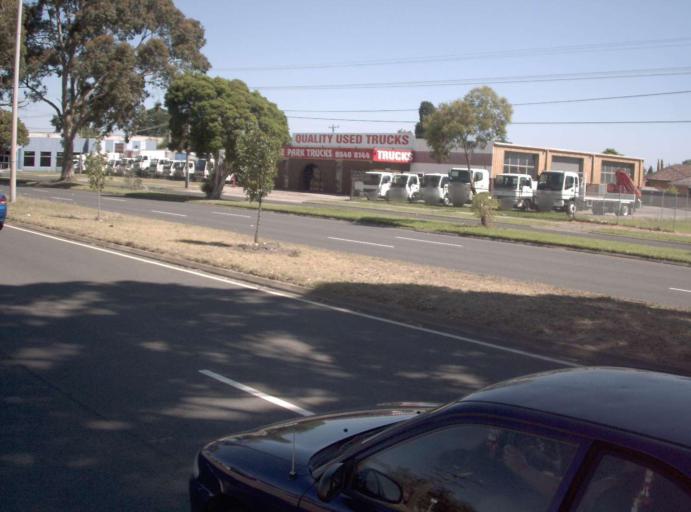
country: AU
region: Victoria
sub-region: Greater Dandenong
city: Noble Park North
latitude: -37.9593
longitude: 145.1861
